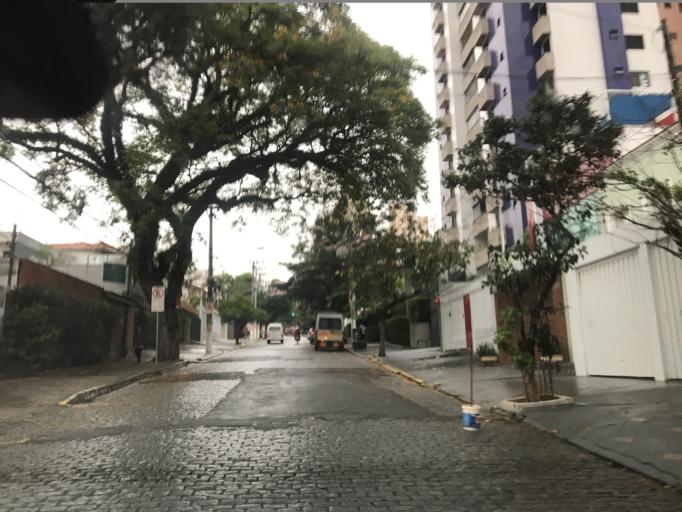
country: BR
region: Sao Paulo
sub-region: Sao Paulo
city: Sao Paulo
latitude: -23.5295
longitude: -46.6859
